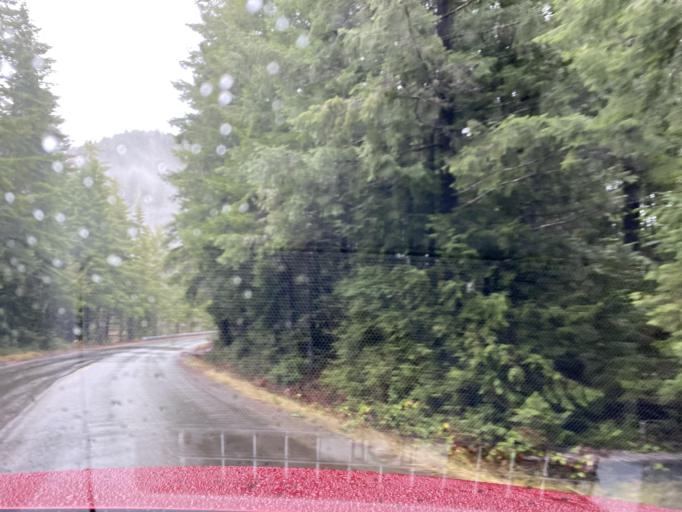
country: US
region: Oregon
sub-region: Lane County
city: Oakridge
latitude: 43.6854
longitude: -122.4428
